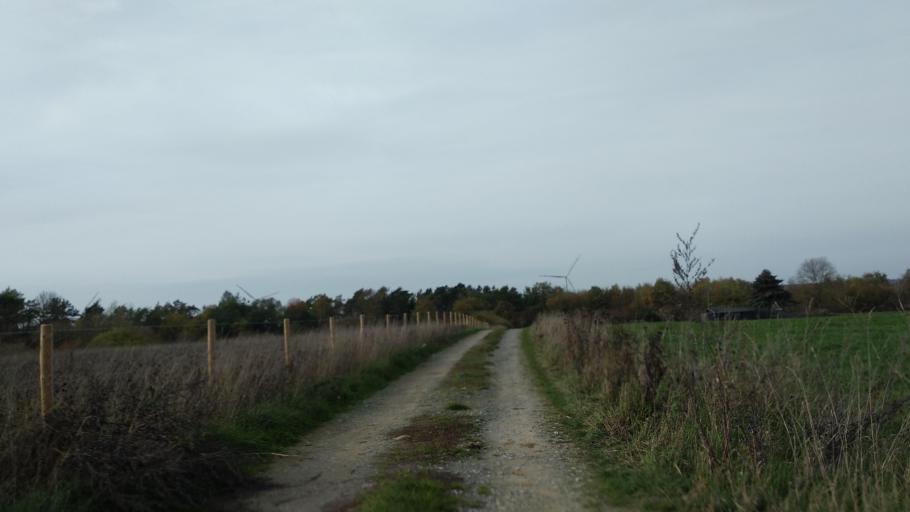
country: DE
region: North Rhine-Westphalia
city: Beverungen
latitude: 51.6912
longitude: 9.3385
